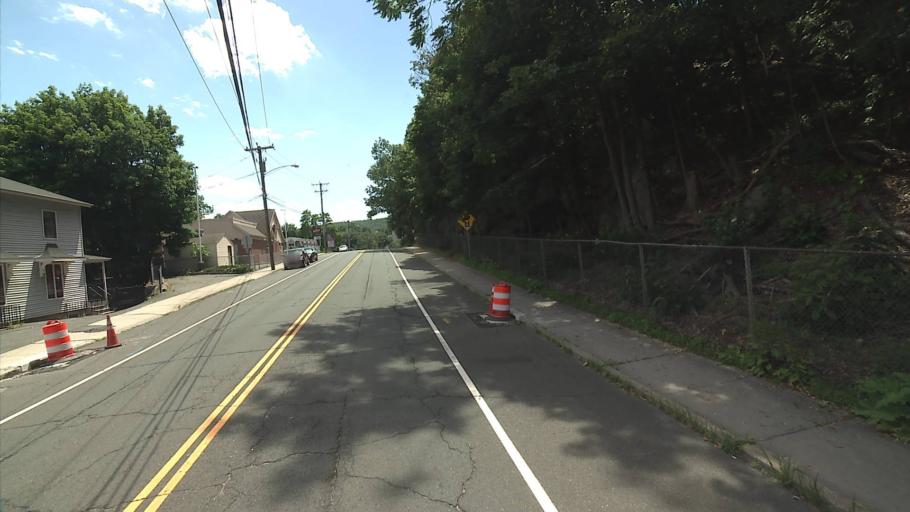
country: US
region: Connecticut
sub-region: New Haven County
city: Naugatuck
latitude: 41.4891
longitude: -73.0571
